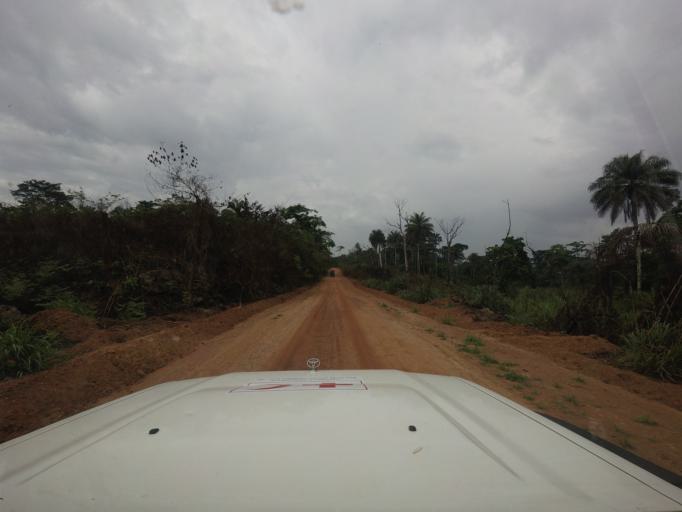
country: SL
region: Eastern Province
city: Buedu
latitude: 8.3093
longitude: -10.1380
